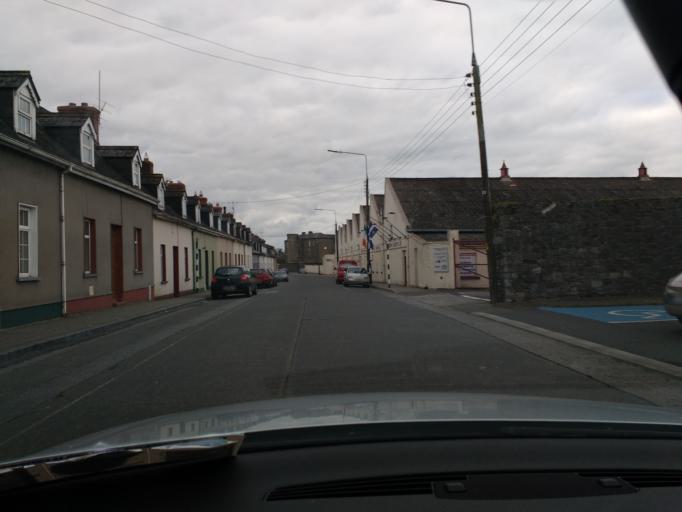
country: IE
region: Leinster
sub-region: Kilkenny
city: Kilkenny
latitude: 52.6560
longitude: -7.2484
